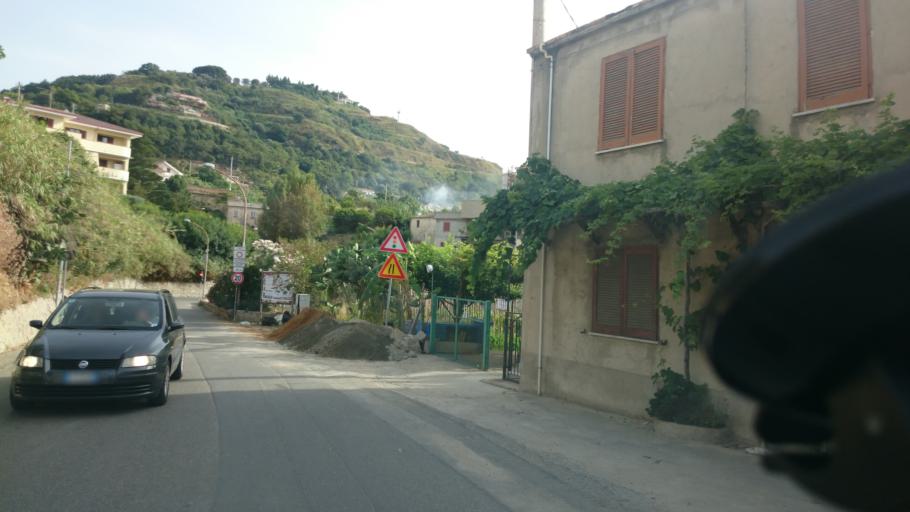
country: IT
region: Calabria
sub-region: Provincia di Vibo-Valentia
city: Tropea
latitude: 38.6753
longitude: 15.9002
